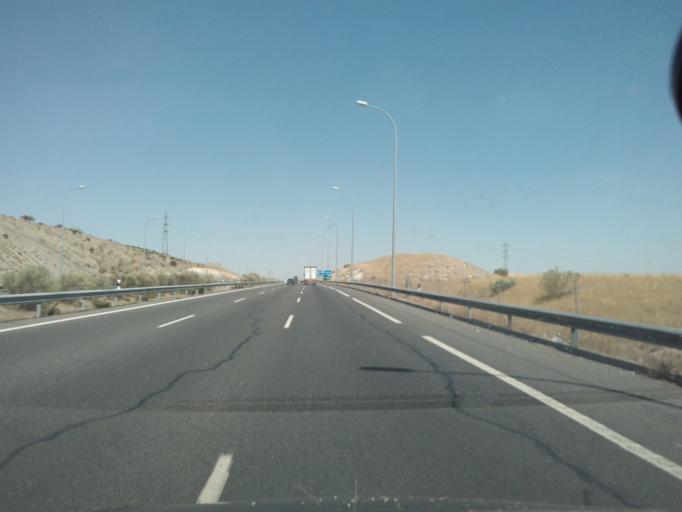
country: ES
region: Madrid
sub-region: Provincia de Madrid
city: Villa de Vallecas
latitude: 40.3397
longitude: -3.6051
